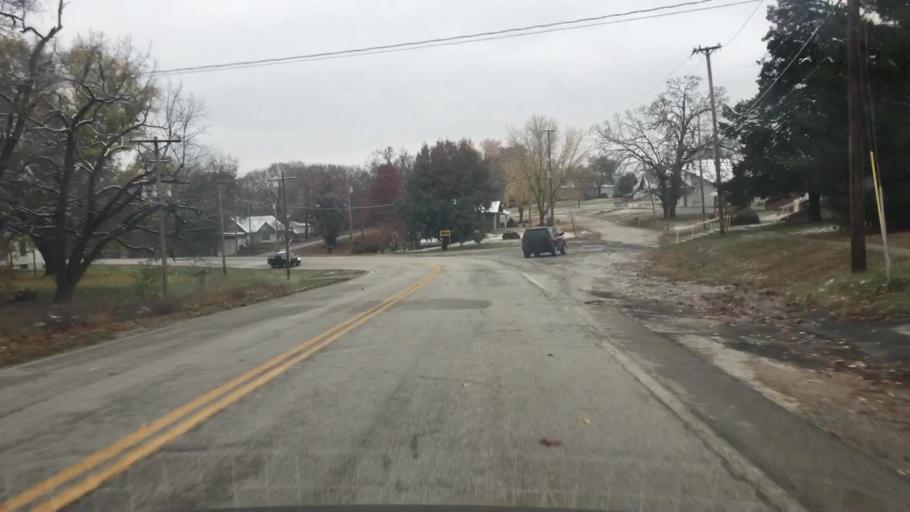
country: US
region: Missouri
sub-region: Saint Clair County
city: Osceola
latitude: 38.0421
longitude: -93.7024
